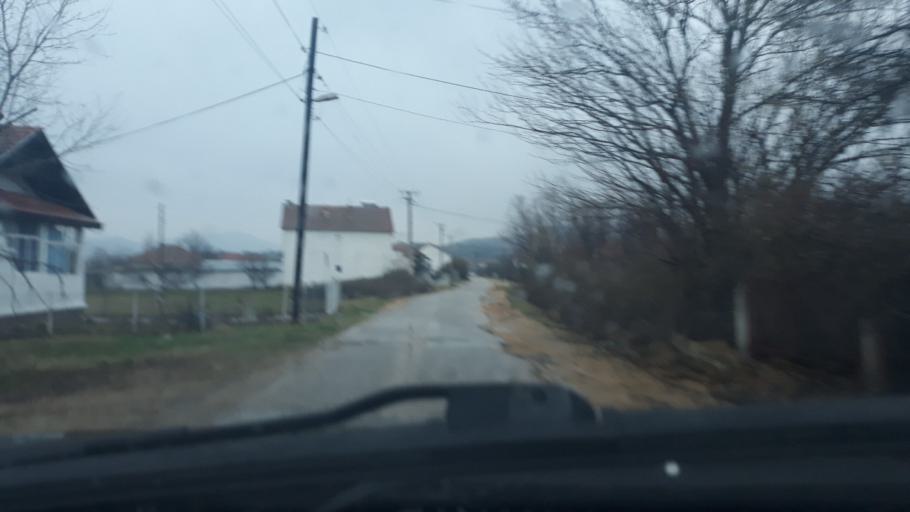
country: MK
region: Bogdanci
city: Bogdanci
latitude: 41.2460
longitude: 22.6117
